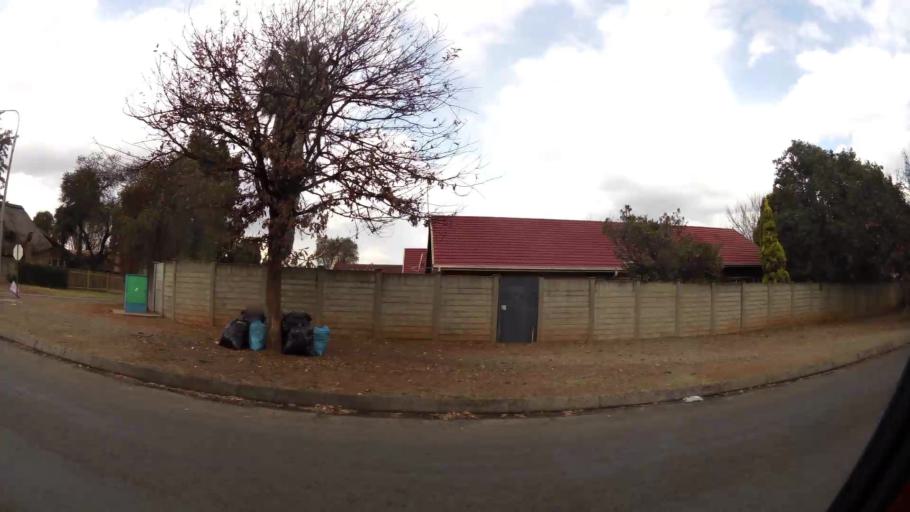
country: ZA
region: Gauteng
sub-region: Sedibeng District Municipality
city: Vanderbijlpark
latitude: -26.7328
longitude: 27.8457
